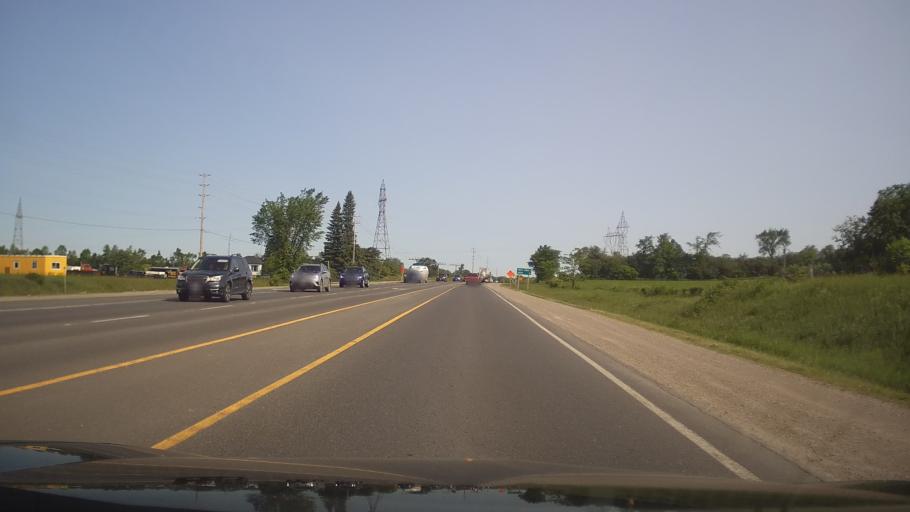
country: CA
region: Ontario
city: Peterborough
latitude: 44.2798
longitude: -78.4198
